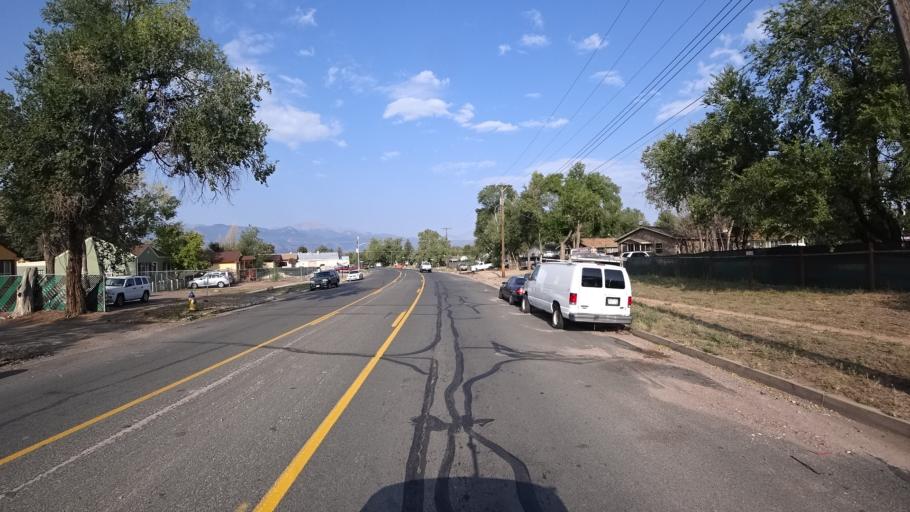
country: US
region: Colorado
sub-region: El Paso County
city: Colorado Springs
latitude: 38.8407
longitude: -104.7791
